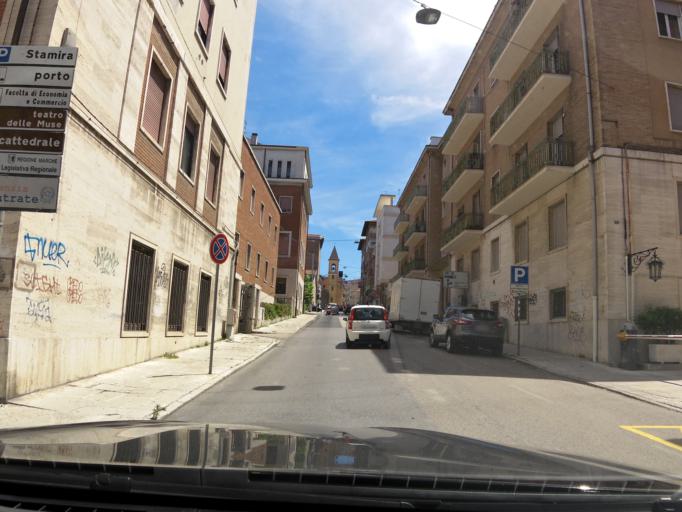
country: IT
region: The Marches
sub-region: Provincia di Ancona
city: Le Grazie di Ancona
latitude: 43.6154
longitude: 13.5164
